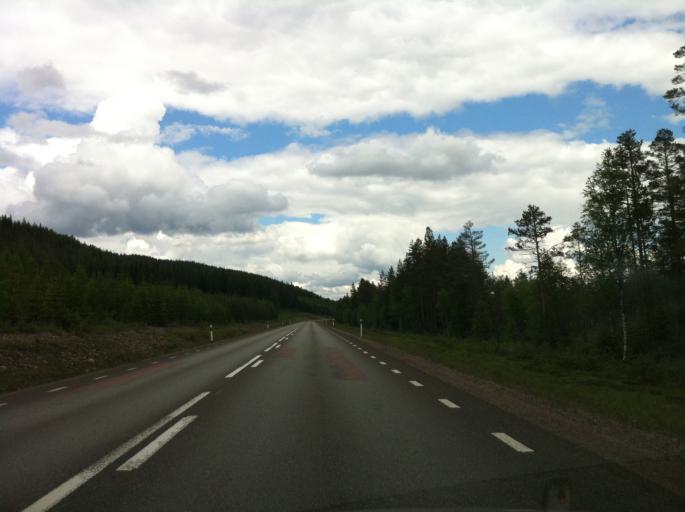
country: SE
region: Dalarna
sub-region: Malung-Saelens kommun
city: Malung
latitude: 60.6163
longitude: 13.6079
